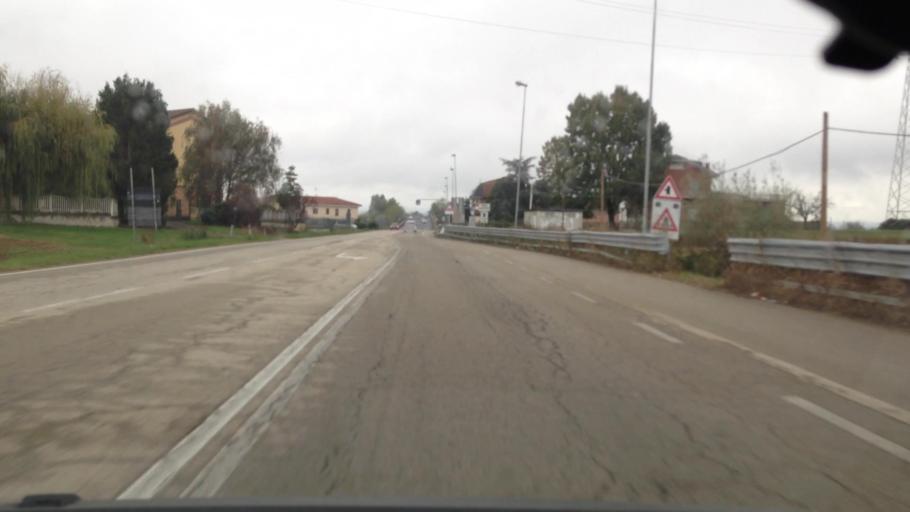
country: IT
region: Piedmont
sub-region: Provincia di Asti
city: Villanova d'Asti
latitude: 44.9606
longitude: 7.9107
